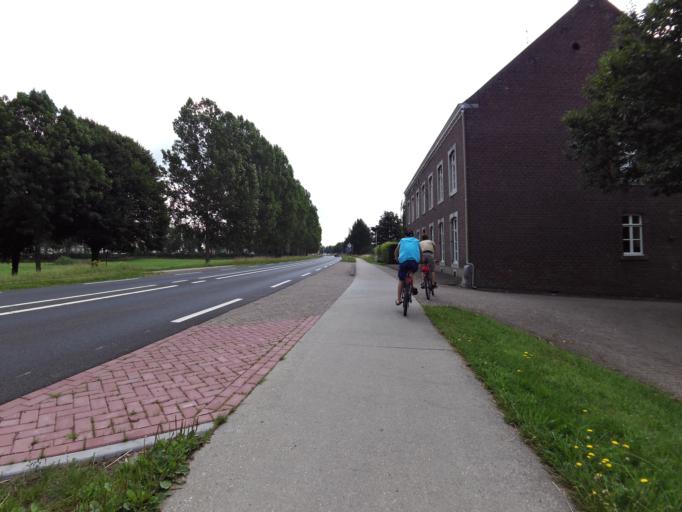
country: NL
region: Limburg
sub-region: Gemeente Voerendaal
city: Ubachsberg
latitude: 50.8128
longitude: 5.9093
